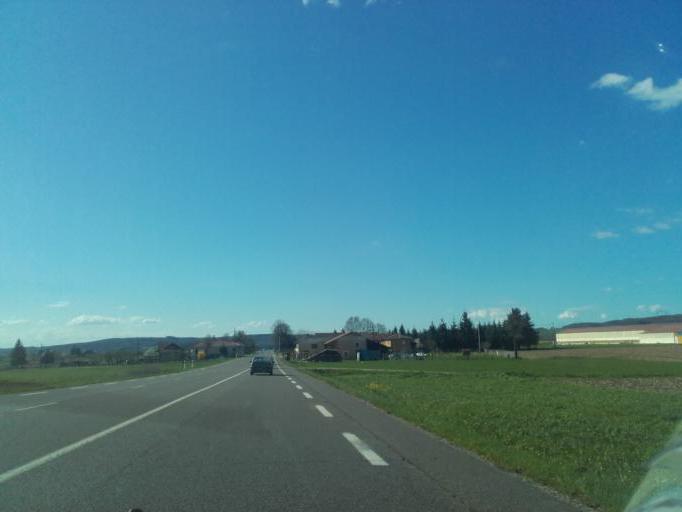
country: FR
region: Rhone-Alpes
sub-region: Departement de l'Isere
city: Saint-Hilaire-de-la-Cote
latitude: 45.4193
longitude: 5.3278
